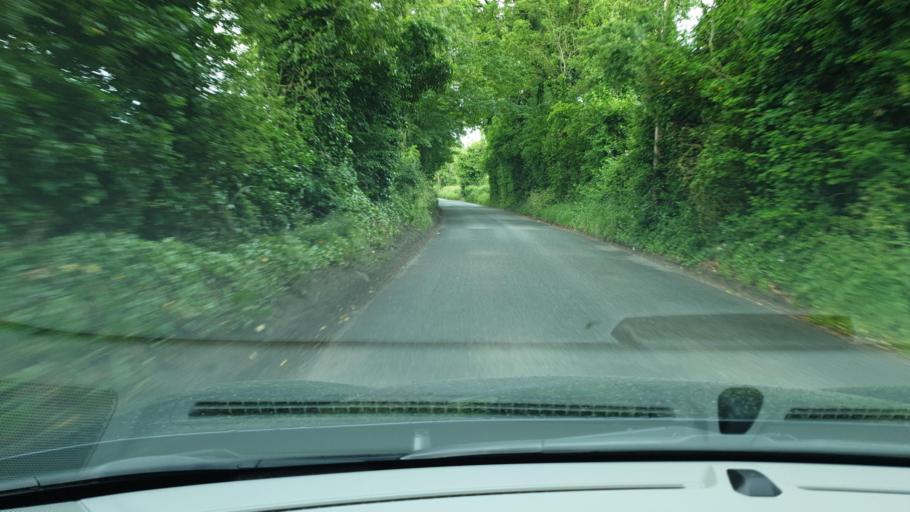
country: IE
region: Leinster
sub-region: An Mhi
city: Ashbourne
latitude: 53.5511
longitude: -6.4005
